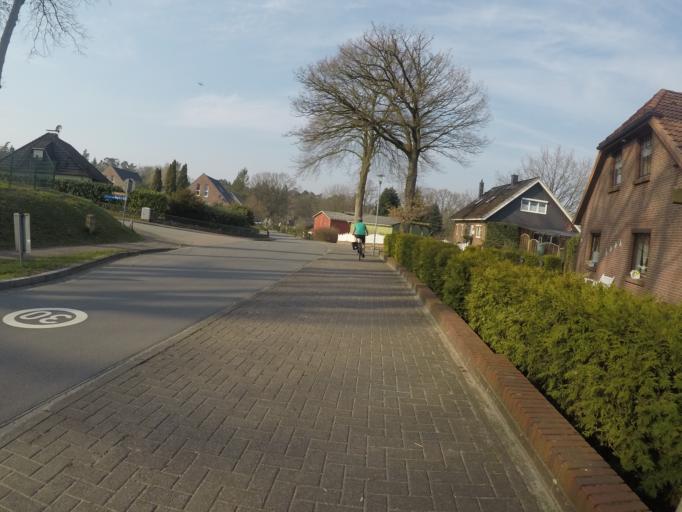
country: DE
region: Schleswig-Holstein
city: Wittenborn
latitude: 53.9228
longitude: 10.2214
